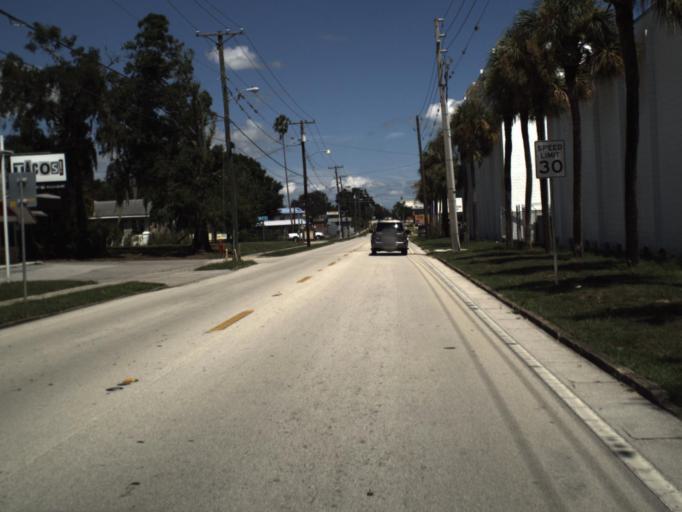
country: US
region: Florida
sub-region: Polk County
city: Frostproof
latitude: 27.7407
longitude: -81.5305
